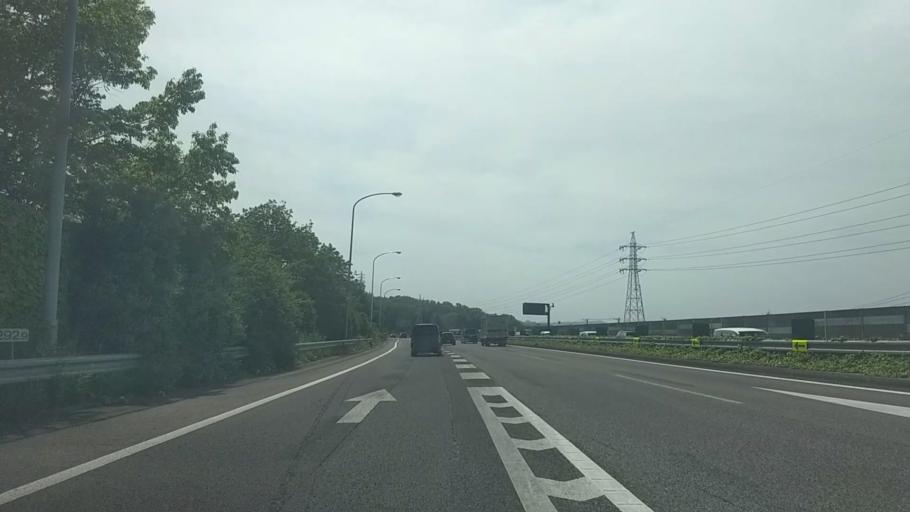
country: JP
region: Aichi
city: Okazaki
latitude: 34.9407
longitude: 137.2013
